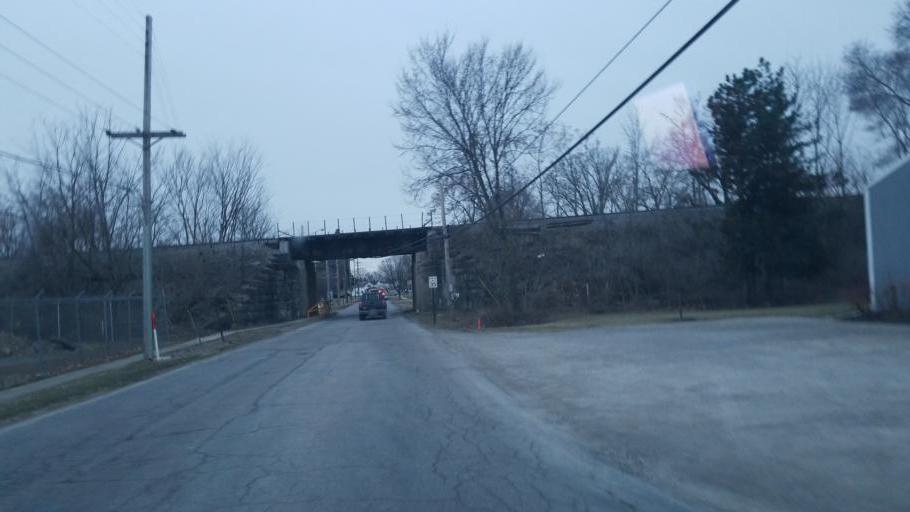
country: US
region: Ohio
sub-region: Defiance County
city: Hicksville
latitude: 41.2983
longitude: -84.7667
